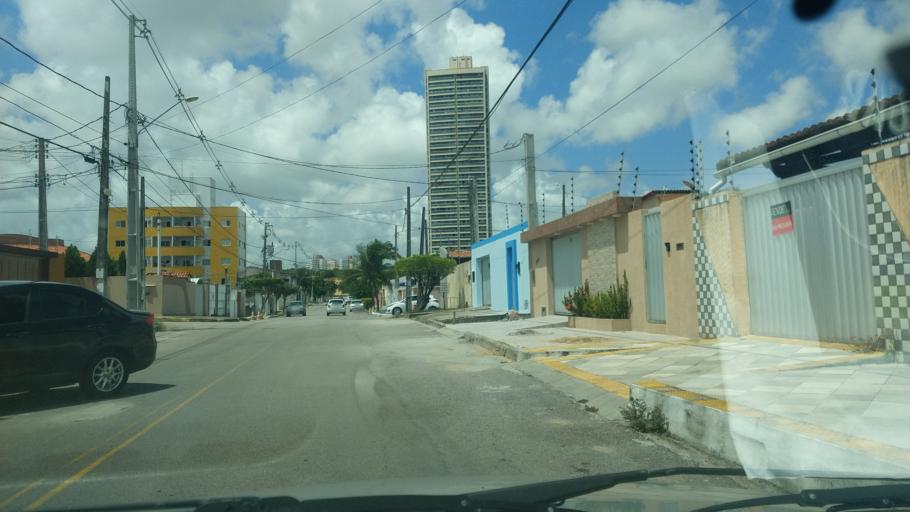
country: BR
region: Rio Grande do Norte
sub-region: Natal
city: Natal
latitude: -5.8681
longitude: -35.1920
